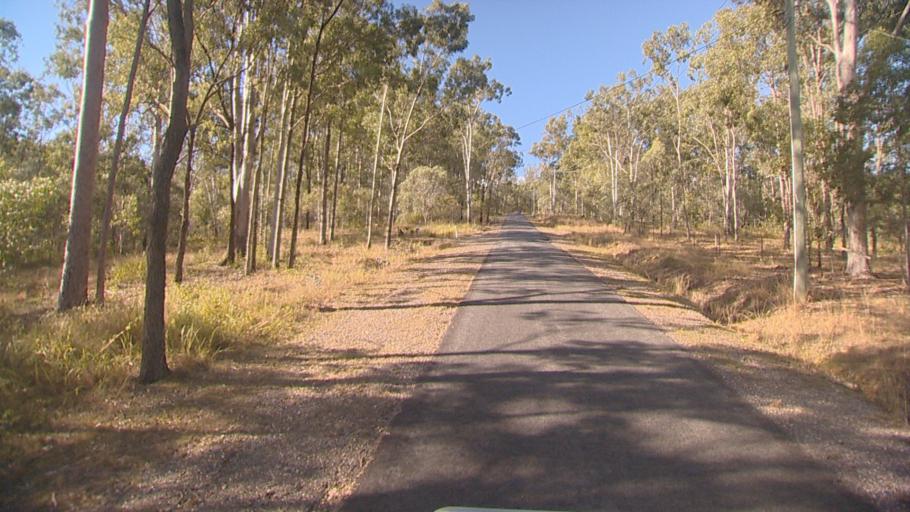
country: AU
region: Queensland
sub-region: Logan
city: Cedar Vale
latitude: -27.8356
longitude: 153.0721
